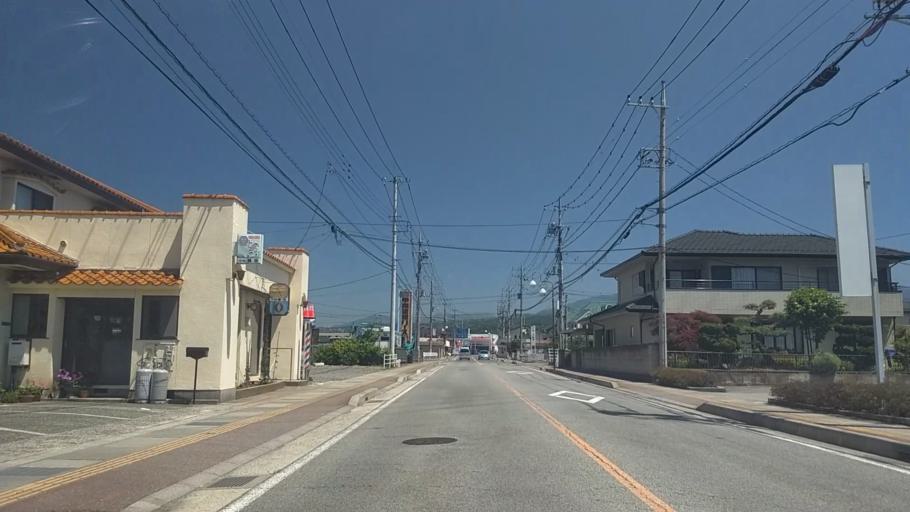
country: JP
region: Yamanashi
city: Nirasaki
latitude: 35.7158
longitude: 138.4484
